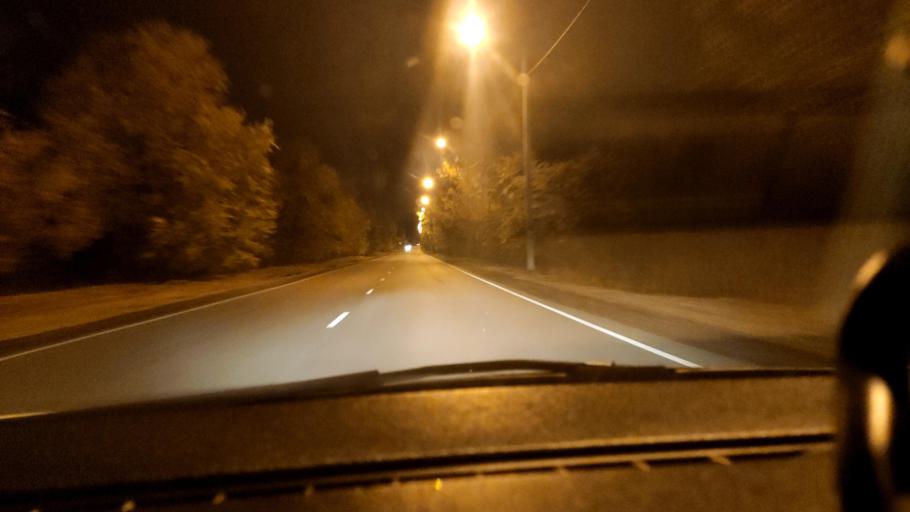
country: RU
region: Voronezj
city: Maslovka
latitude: 51.5930
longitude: 39.1758
